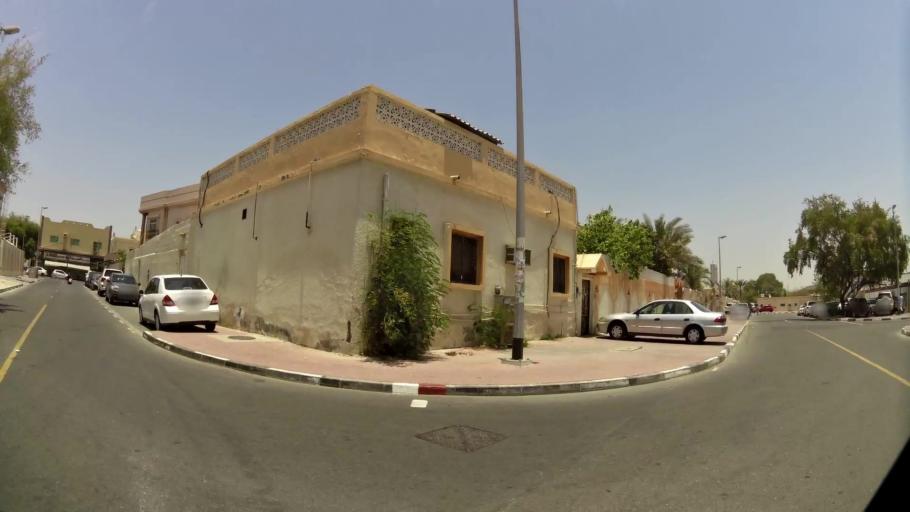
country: AE
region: Ash Shariqah
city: Sharjah
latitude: 25.2393
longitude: 55.2838
